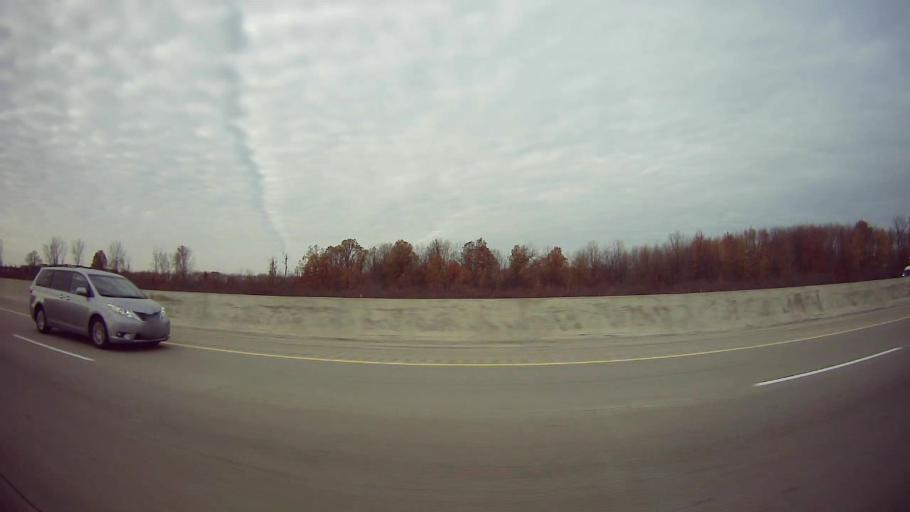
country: US
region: Michigan
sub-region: Wayne County
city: Woodhaven
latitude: 42.1594
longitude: -83.2425
